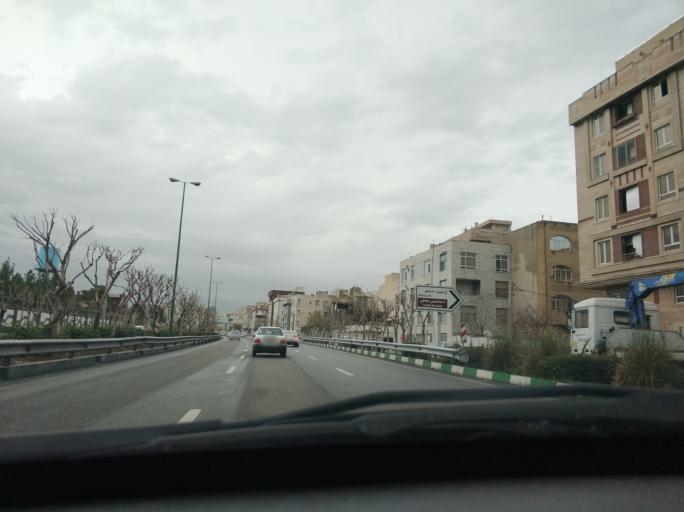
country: IR
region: Tehran
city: Tehran
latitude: 35.7107
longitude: 51.4439
